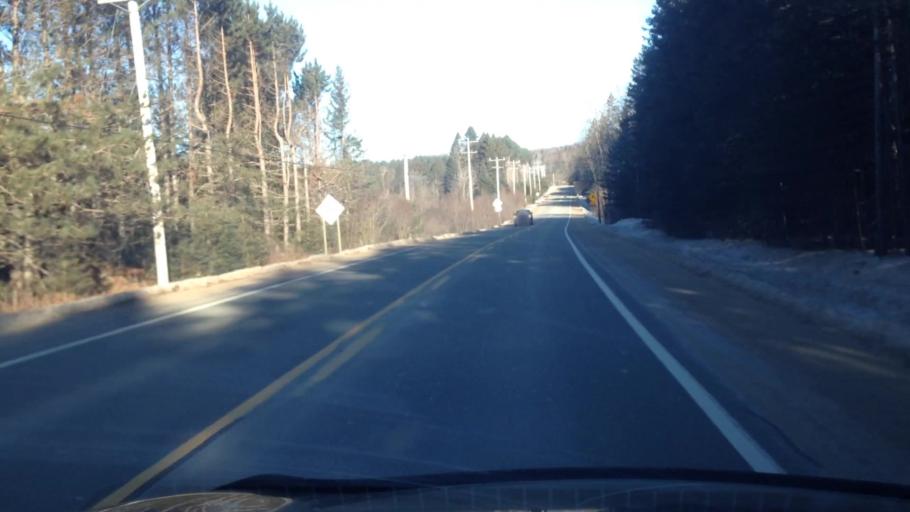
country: CA
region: Quebec
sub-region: Laurentides
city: Mont-Tremblant
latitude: 46.0026
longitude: -74.6213
